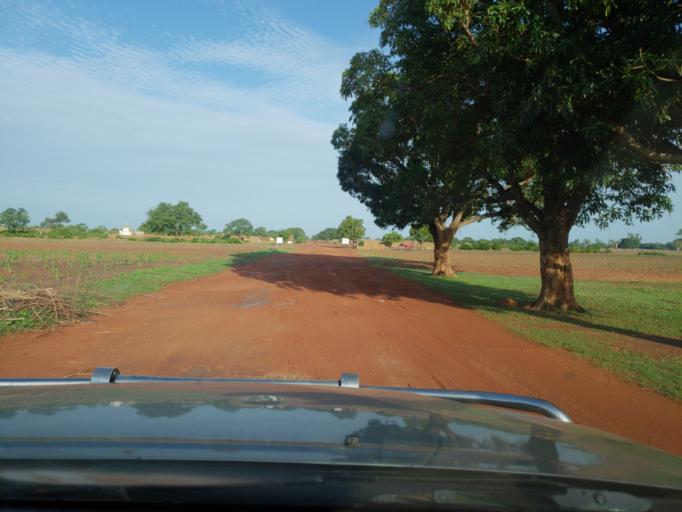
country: ML
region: Sikasso
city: Koutiala
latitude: 12.4296
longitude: -5.6082
